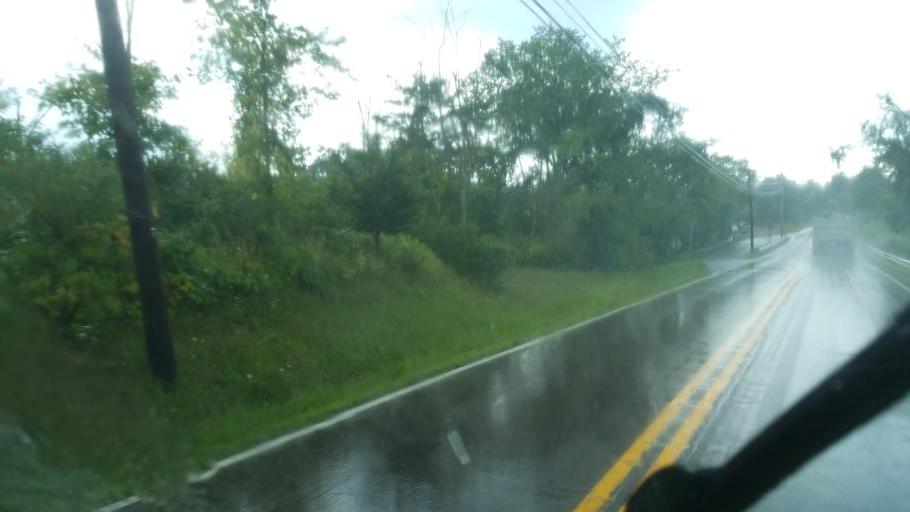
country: US
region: West Virginia
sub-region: Mineral County
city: Fort Ashby
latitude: 39.5425
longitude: -78.6126
